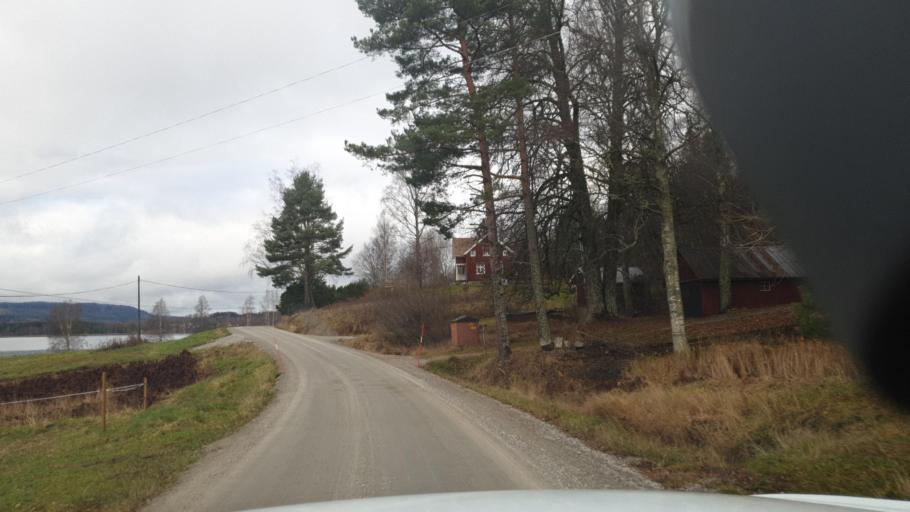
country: SE
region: Vaermland
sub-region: Arvika Kommun
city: Arvika
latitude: 59.7294
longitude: 12.8341
